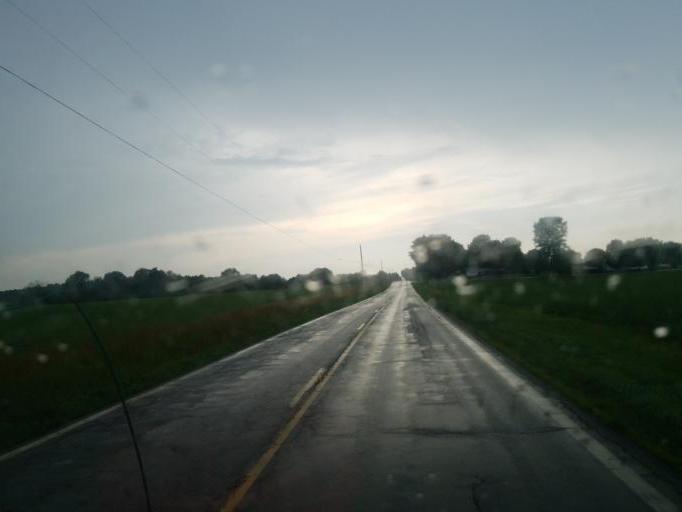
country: US
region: Ohio
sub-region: Wayne County
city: Creston
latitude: 40.9458
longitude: -81.8457
